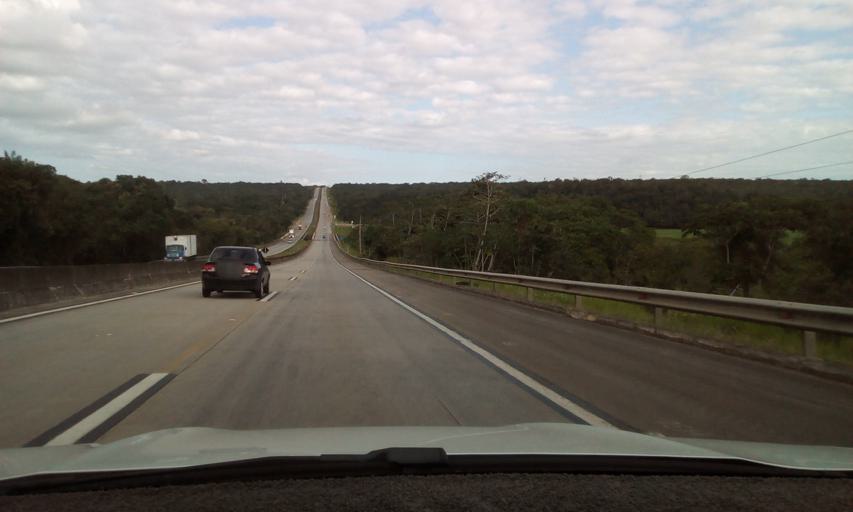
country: BR
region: Paraiba
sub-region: Mamanguape
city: Mamanguape
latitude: -6.9365
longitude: -35.1006
